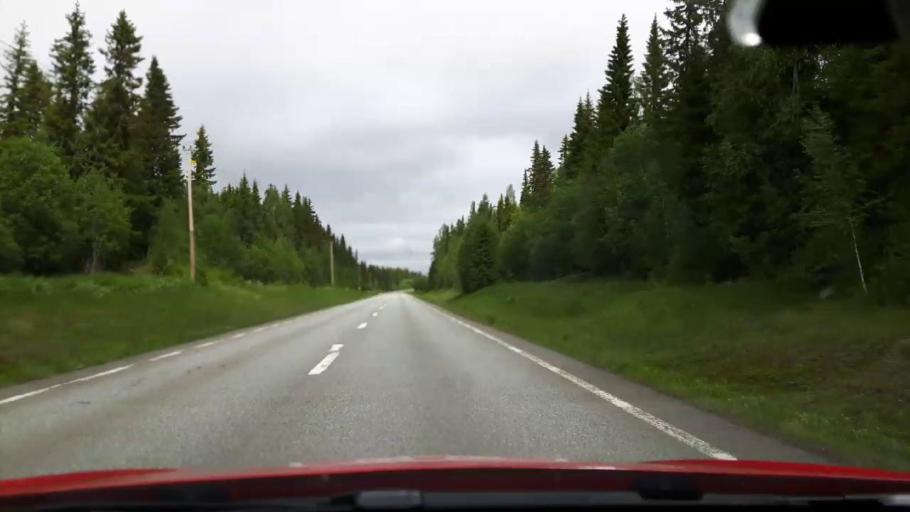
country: SE
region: Jaemtland
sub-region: Krokoms Kommun
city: Krokom
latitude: 63.4888
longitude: 14.5060
